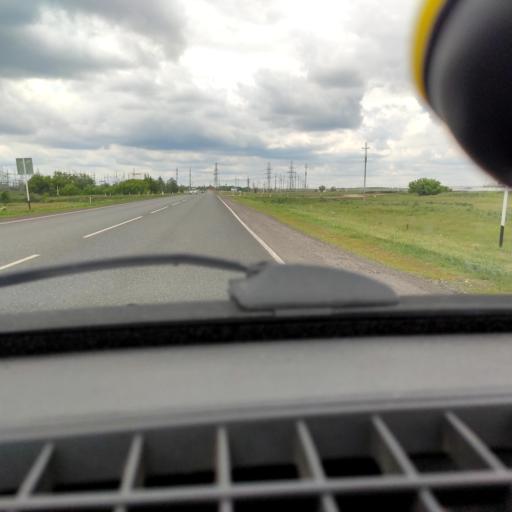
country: RU
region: Samara
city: Povolzhskiy
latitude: 53.6524
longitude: 49.6896
